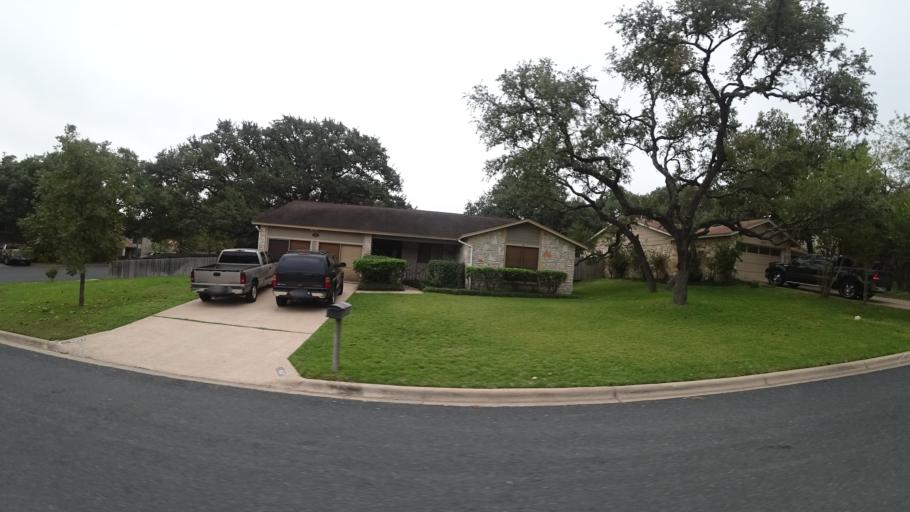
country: US
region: Texas
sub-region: Travis County
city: Austin
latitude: 30.3480
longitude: -97.6894
